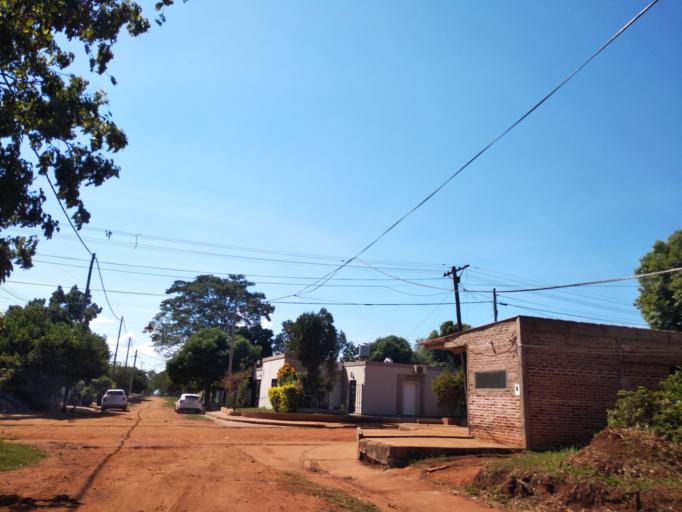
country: AR
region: Misiones
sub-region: Departamento de Capital
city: Posadas
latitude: -27.4277
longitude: -55.8847
